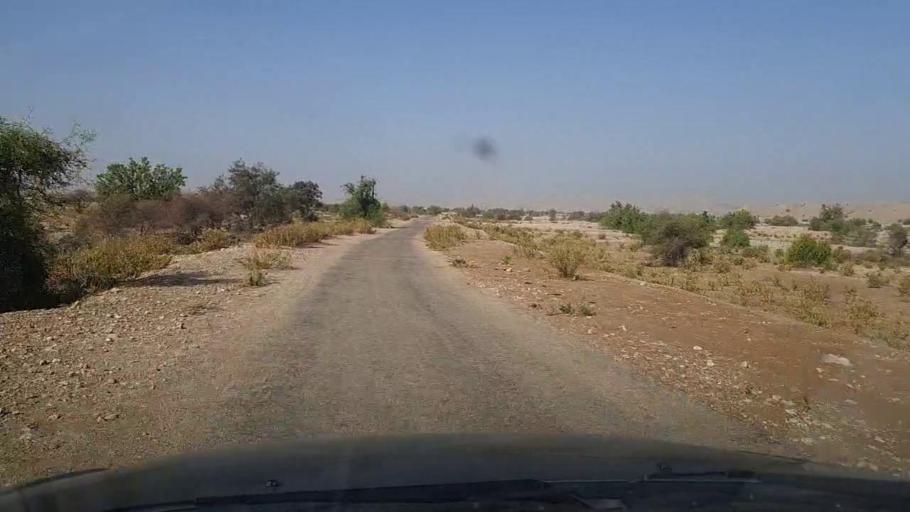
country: PK
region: Sindh
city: Sann
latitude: 25.8881
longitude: 67.9869
